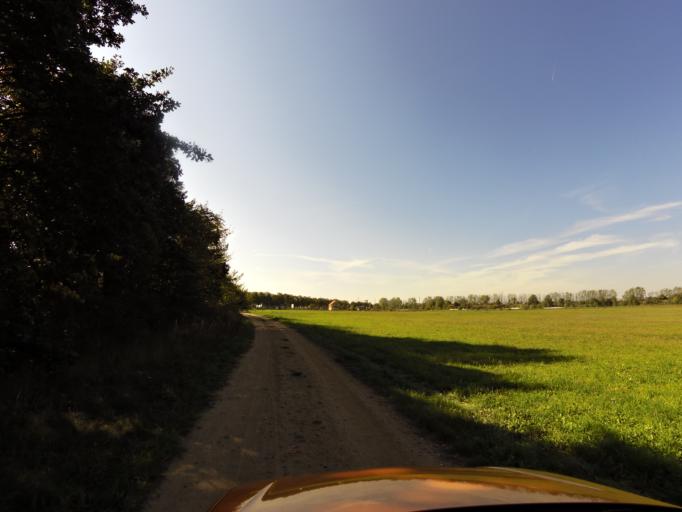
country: DE
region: Brandenburg
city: Grossbeeren
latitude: 52.3543
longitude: 13.3002
